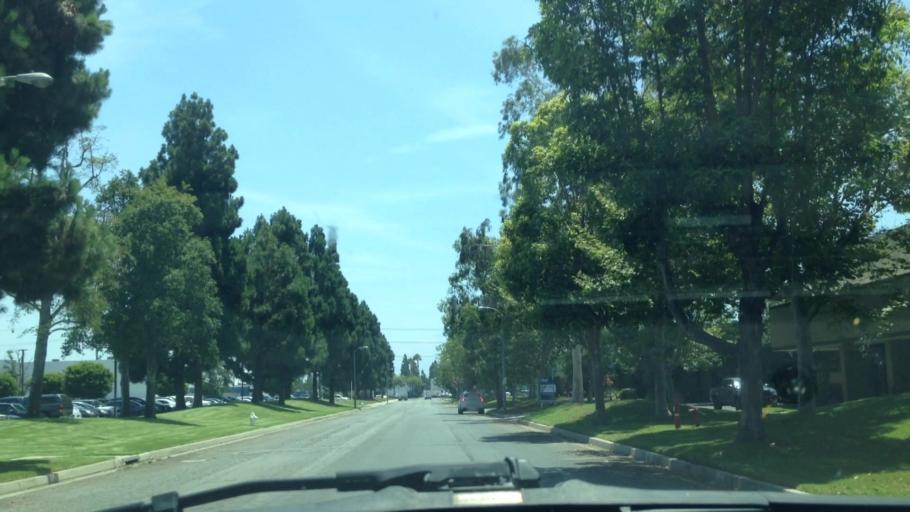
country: US
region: California
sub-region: Orange County
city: Fountain Valley
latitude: 33.7053
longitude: -117.9220
